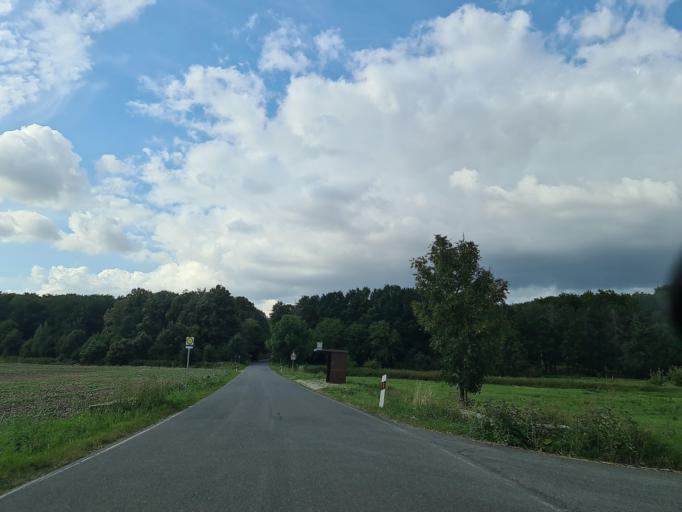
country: DE
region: Thuringia
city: Walpernhain
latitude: 51.0439
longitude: 11.9684
